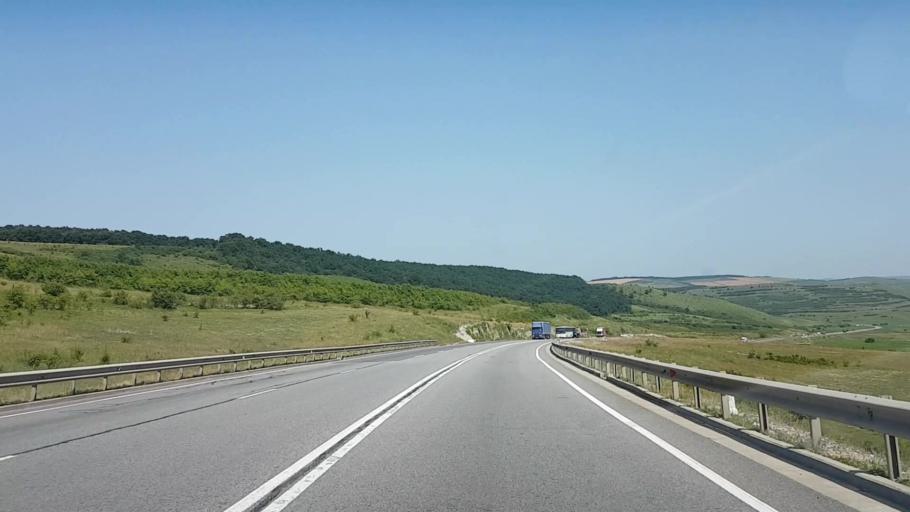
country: RO
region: Cluj
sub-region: Comuna Feleacu
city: Gheorghieni
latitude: 46.7313
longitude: 23.6760
